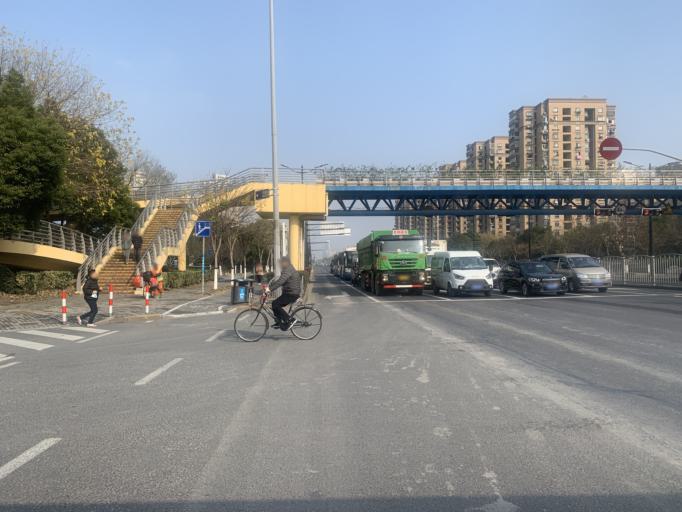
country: CN
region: Shanghai Shi
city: Huamu
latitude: 31.1820
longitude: 121.5161
